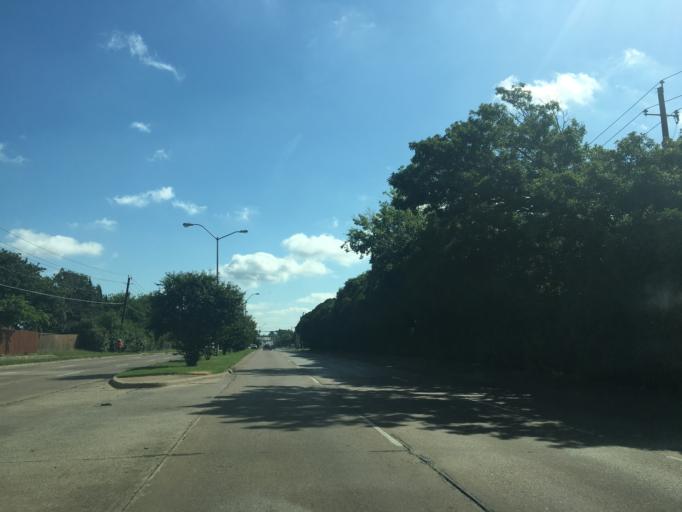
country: US
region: Texas
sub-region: Dallas County
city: Garland
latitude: 32.8495
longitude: -96.6564
